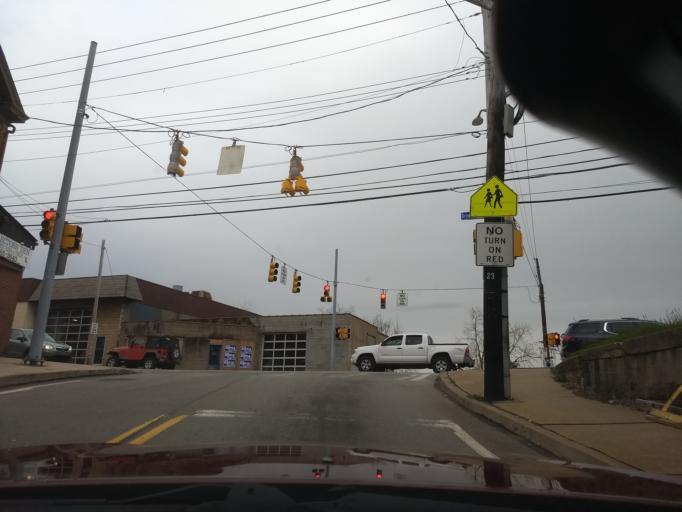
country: US
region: Pennsylvania
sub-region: Allegheny County
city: Brentwood
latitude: 40.3875
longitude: -79.9837
